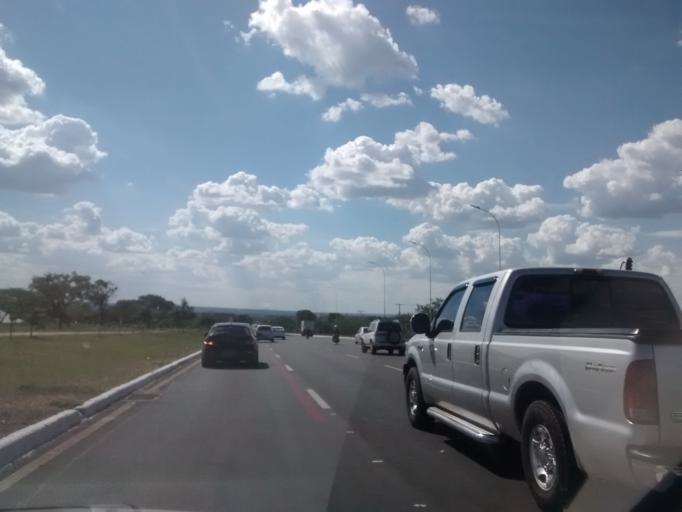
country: BR
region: Federal District
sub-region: Brasilia
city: Brasilia
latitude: -15.7805
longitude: -47.9222
